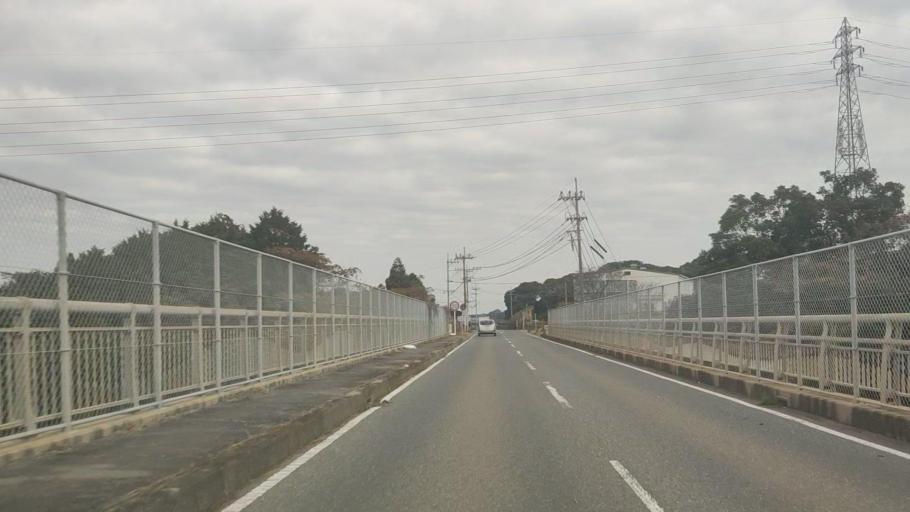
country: JP
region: Nagasaki
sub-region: Isahaya-shi
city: Isahaya
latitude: 32.8078
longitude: 130.1695
